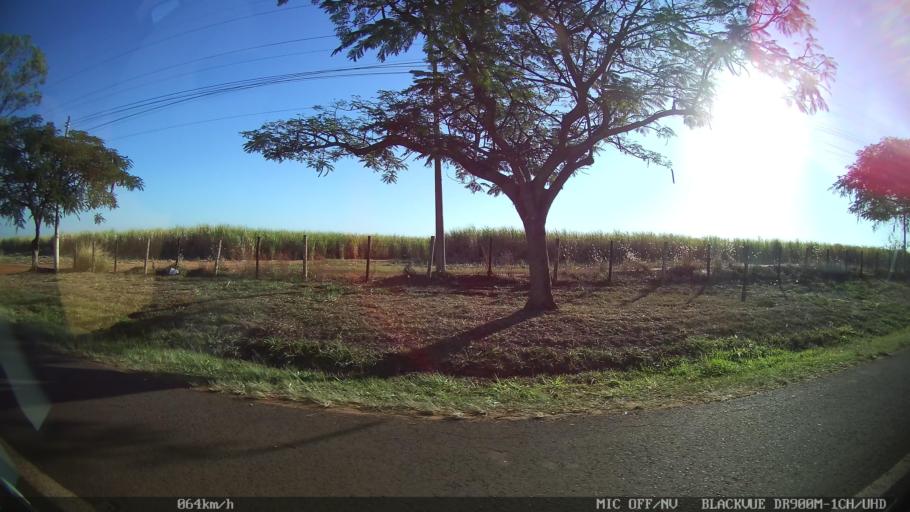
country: BR
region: Sao Paulo
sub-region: Guapiacu
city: Guapiacu
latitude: -20.7762
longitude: -49.2249
